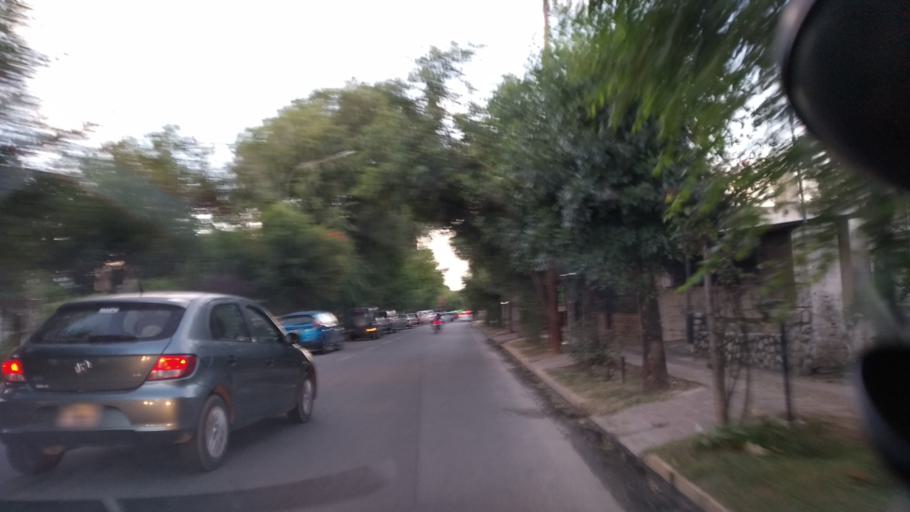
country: AR
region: Cordoba
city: Villa Las Rosas
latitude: -31.9502
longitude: -65.0526
